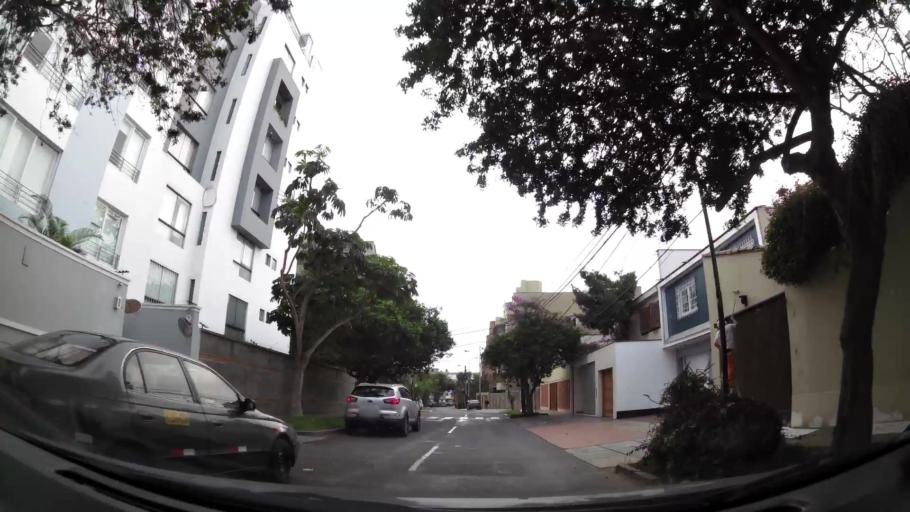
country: PE
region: Lima
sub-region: Lima
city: San Isidro
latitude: -12.1059
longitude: -77.0461
